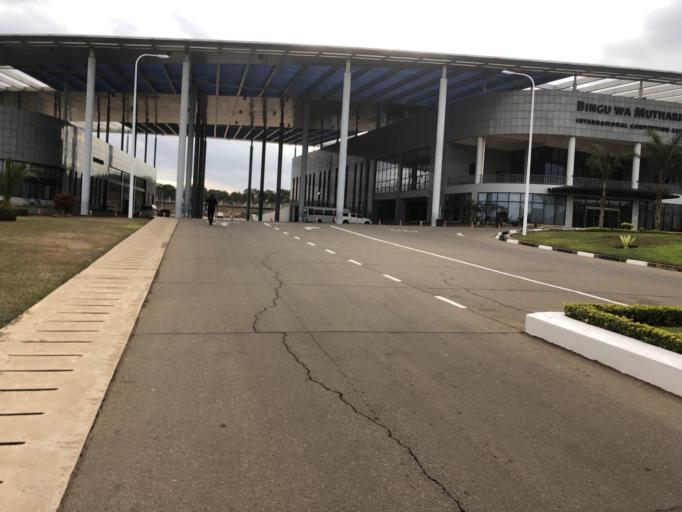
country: MW
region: Central Region
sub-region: Lilongwe District
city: Lilongwe
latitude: -13.9547
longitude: 33.7939
